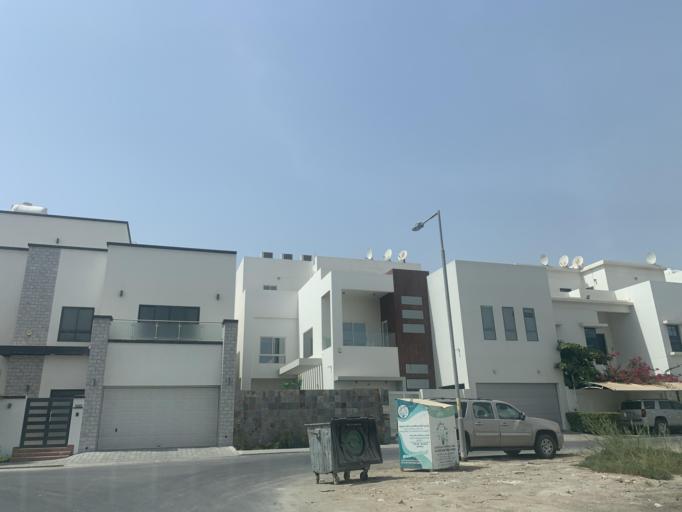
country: BH
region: Northern
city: Madinat `Isa
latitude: 26.1950
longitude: 50.4922
